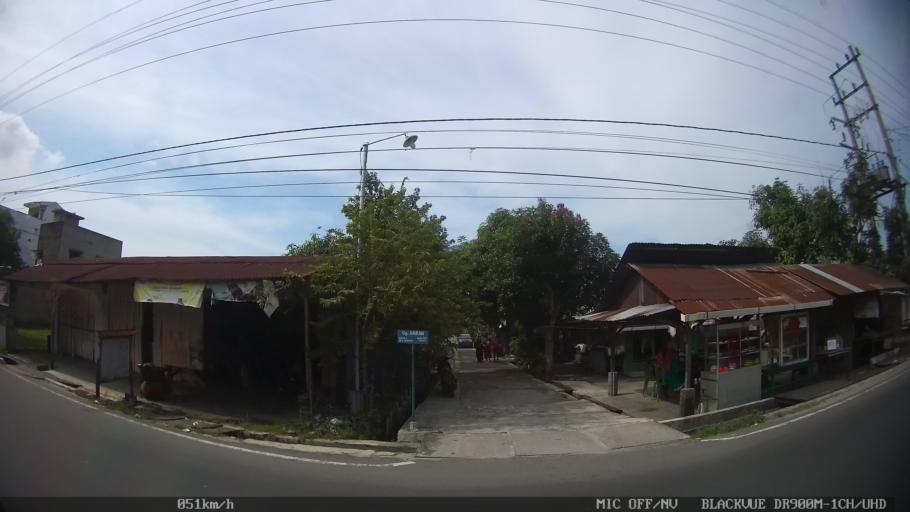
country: ID
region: North Sumatra
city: Percut
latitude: 3.6073
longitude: 98.7772
